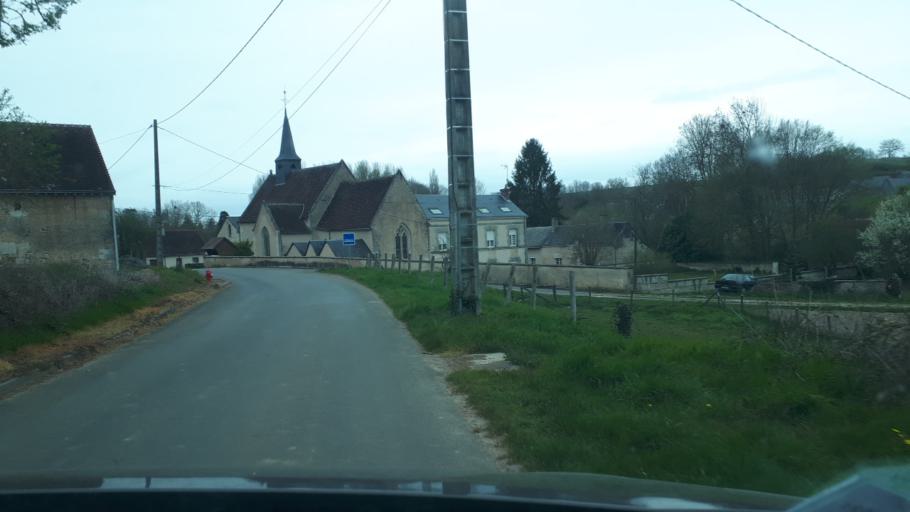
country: FR
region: Centre
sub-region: Departement du Loir-et-Cher
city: Lunay
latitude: 47.7618
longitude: 0.9228
